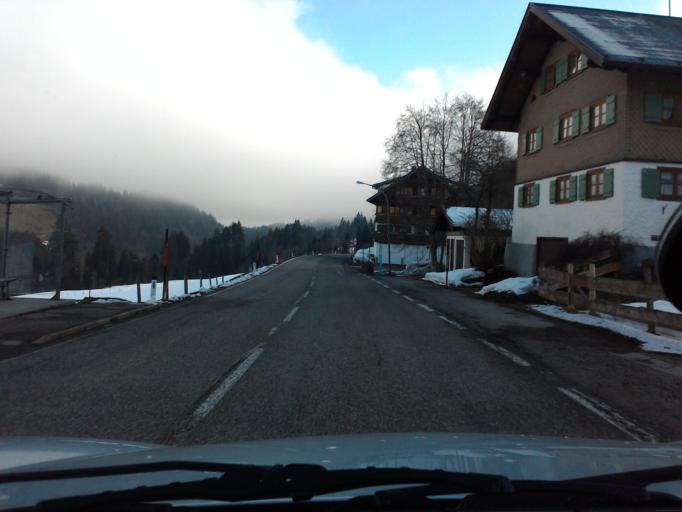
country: DE
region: Bavaria
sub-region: Swabia
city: Oberstdorf
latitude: 47.3789
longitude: 10.2166
